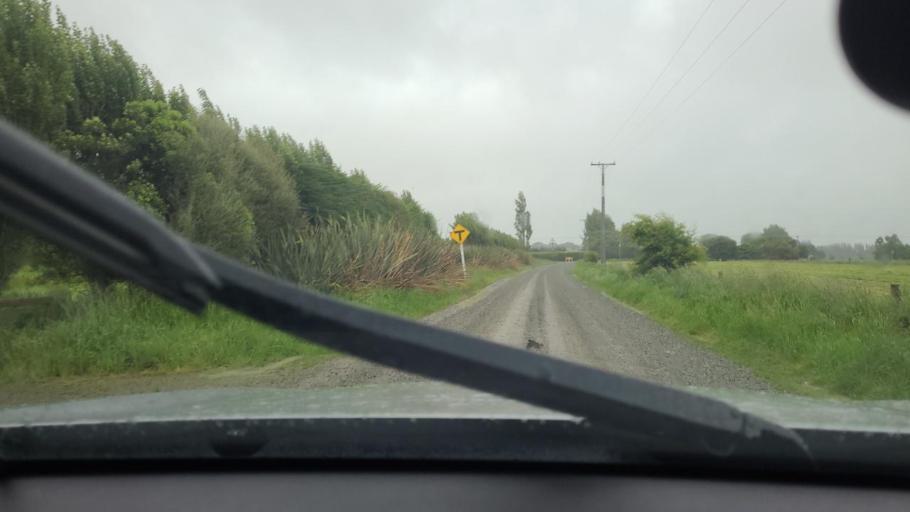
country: NZ
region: Southland
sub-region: Southland District
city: Winton
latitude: -46.1595
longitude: 168.3355
